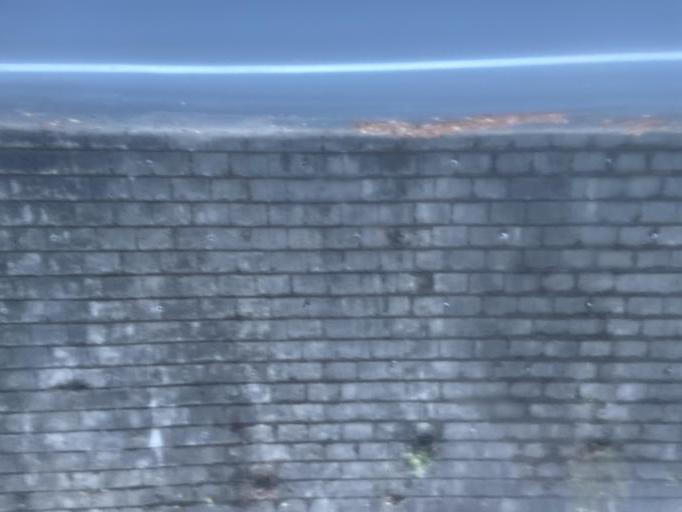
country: JP
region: Saitama
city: Yorii
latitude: 36.0753
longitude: 139.1787
